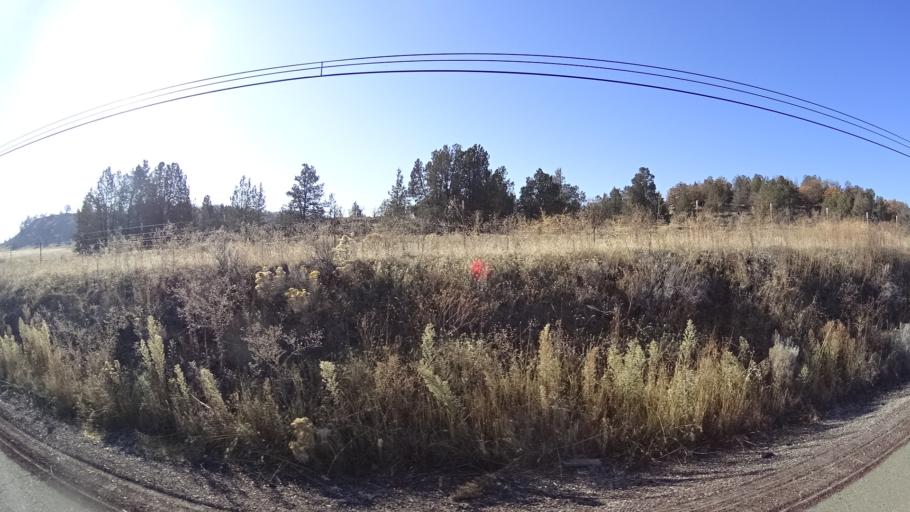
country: US
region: California
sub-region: Siskiyou County
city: Montague
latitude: 41.7105
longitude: -122.5794
